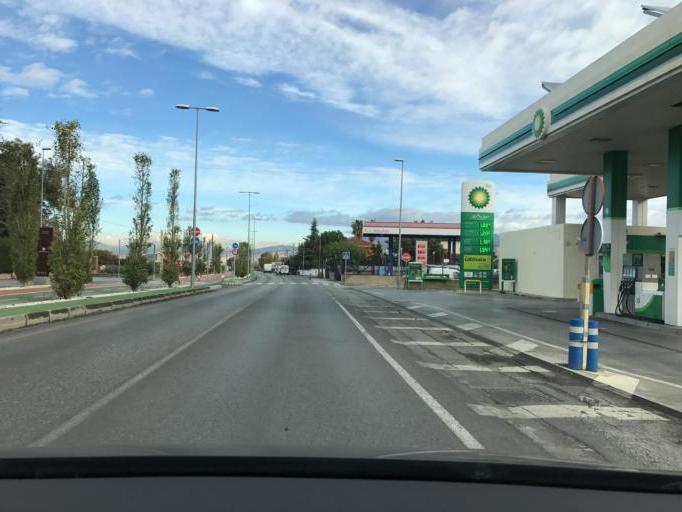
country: ES
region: Andalusia
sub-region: Provincia de Granada
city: Ogijares
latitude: 37.1284
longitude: -3.6036
